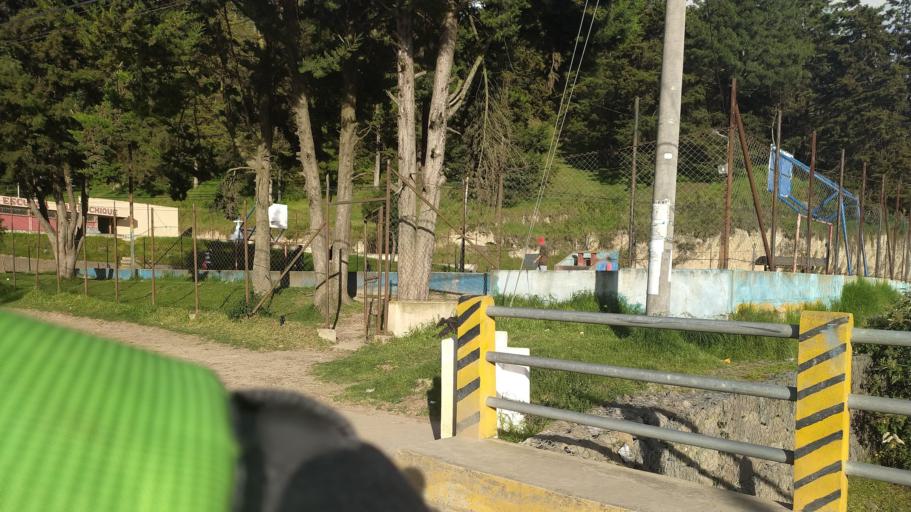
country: GT
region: Quetzaltenango
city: Salcaja
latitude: 14.8729
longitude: -91.4586
